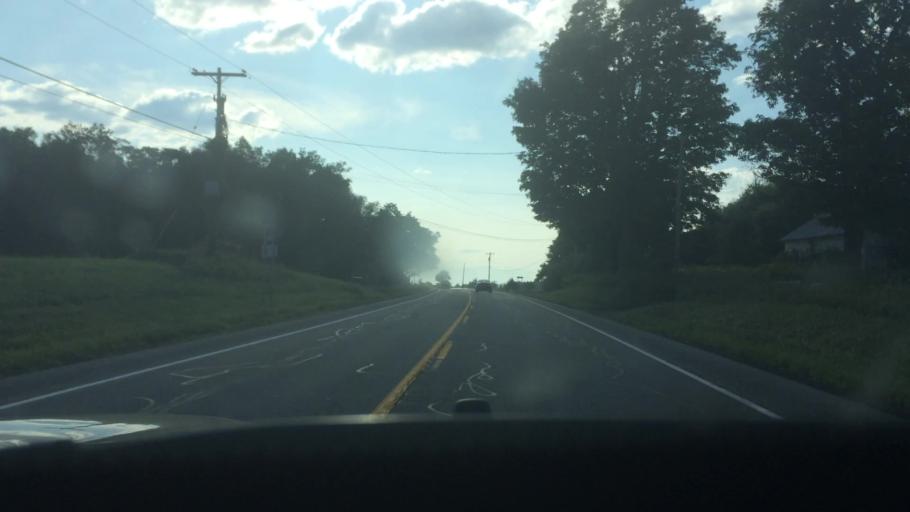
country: US
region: New York
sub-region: St. Lawrence County
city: Potsdam
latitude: 44.6897
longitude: -74.7442
